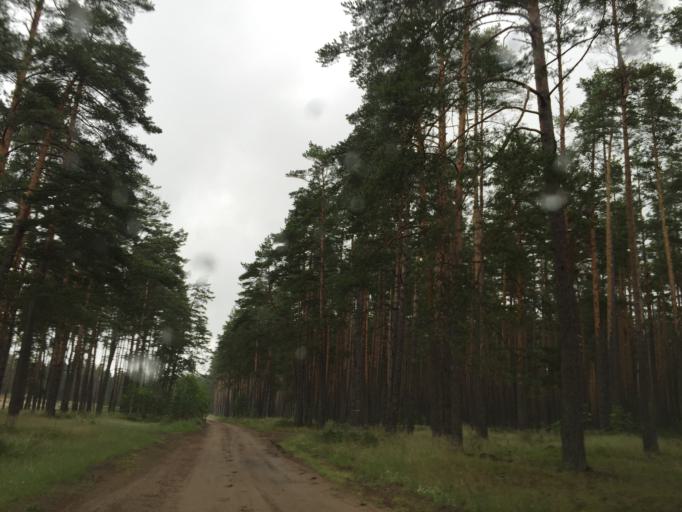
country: LV
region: Riga
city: Jaunciems
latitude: 57.0572
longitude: 24.2018
